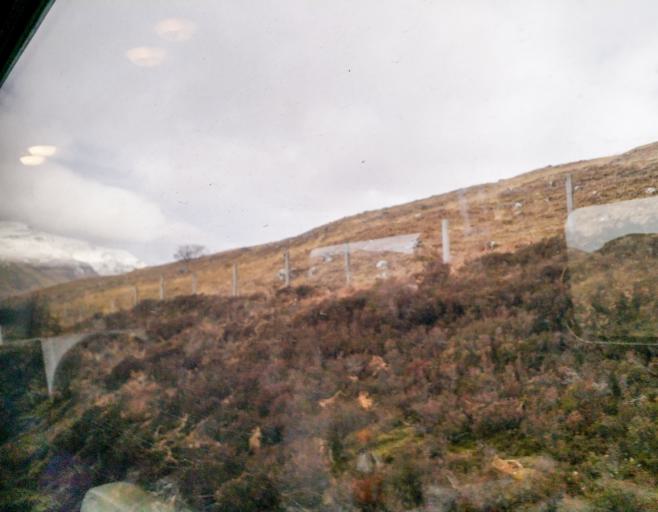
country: GB
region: Scotland
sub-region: Highland
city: Spean Bridge
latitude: 56.7779
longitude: -4.7316
